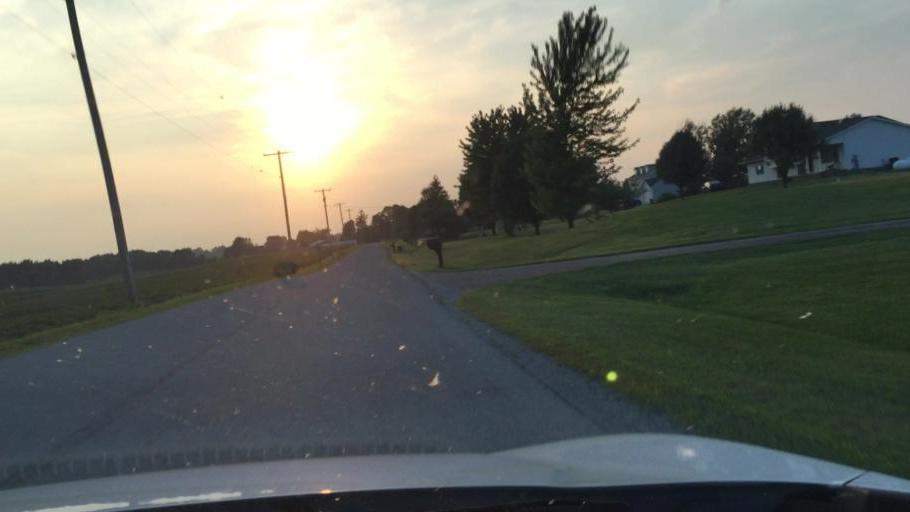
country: US
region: Ohio
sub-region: Madison County
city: Choctaw Lake
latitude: 39.9474
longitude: -83.5609
